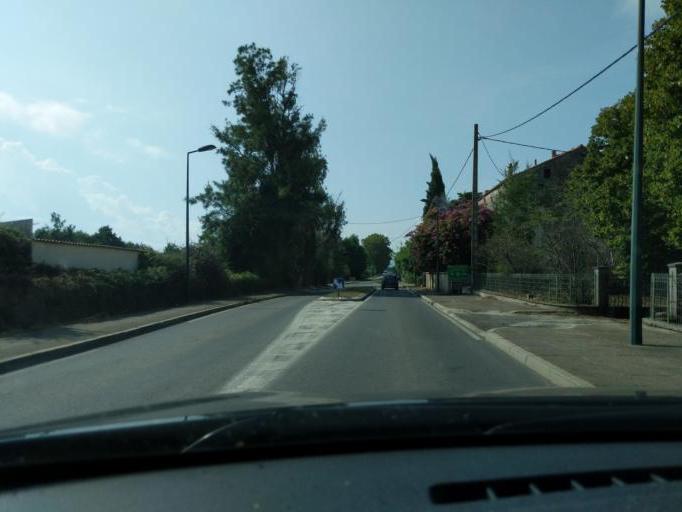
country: FR
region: Corsica
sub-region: Departement de la Haute-Corse
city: Ghisonaccia
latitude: 41.9837
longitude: 9.4007
